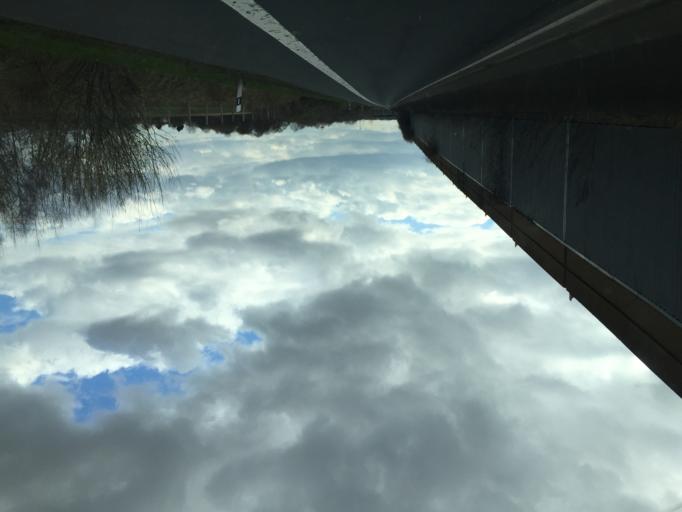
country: DE
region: Lower Saxony
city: Peine
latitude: 52.3369
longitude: 10.2576
